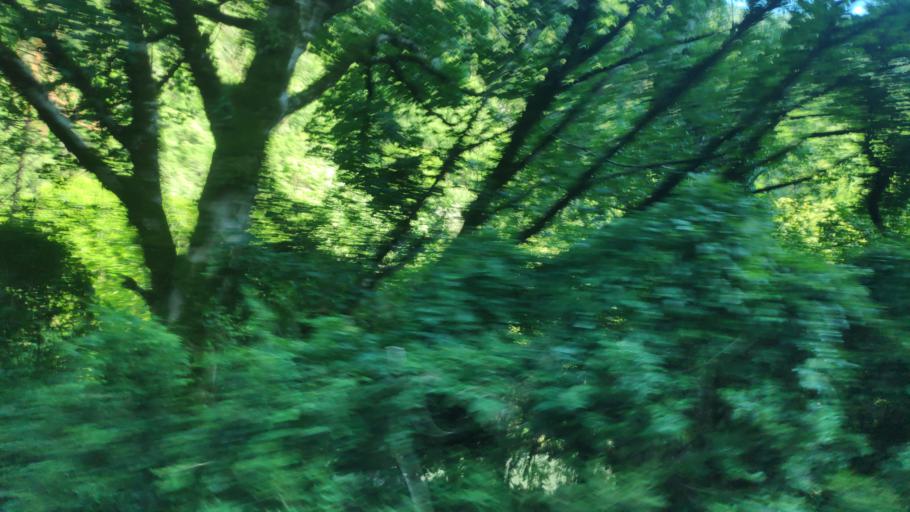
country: GE
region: Abkhazia
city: Gagra
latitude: 43.3580
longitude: 40.4287
